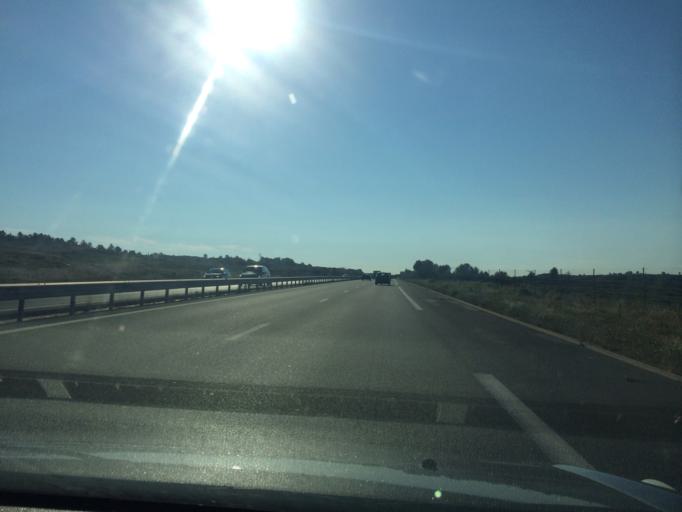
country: FR
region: Languedoc-Roussillon
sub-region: Departement de l'Herault
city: Murviel-les-Montpellier
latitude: 43.6329
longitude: 3.7326
